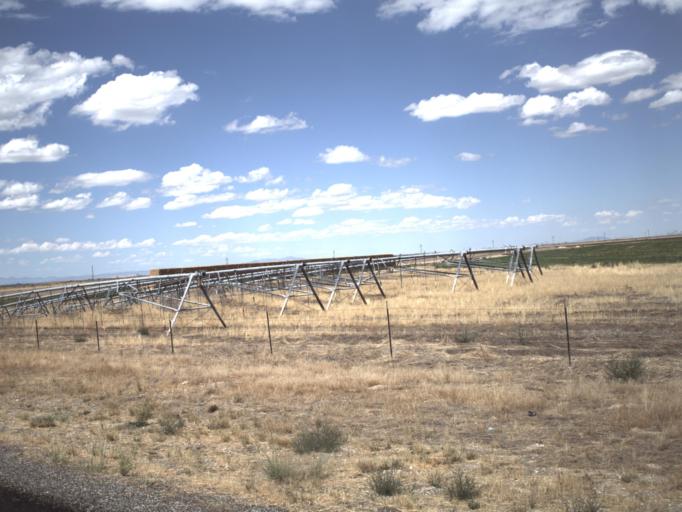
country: US
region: Utah
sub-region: Millard County
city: Fillmore
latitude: 39.1181
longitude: -112.3389
